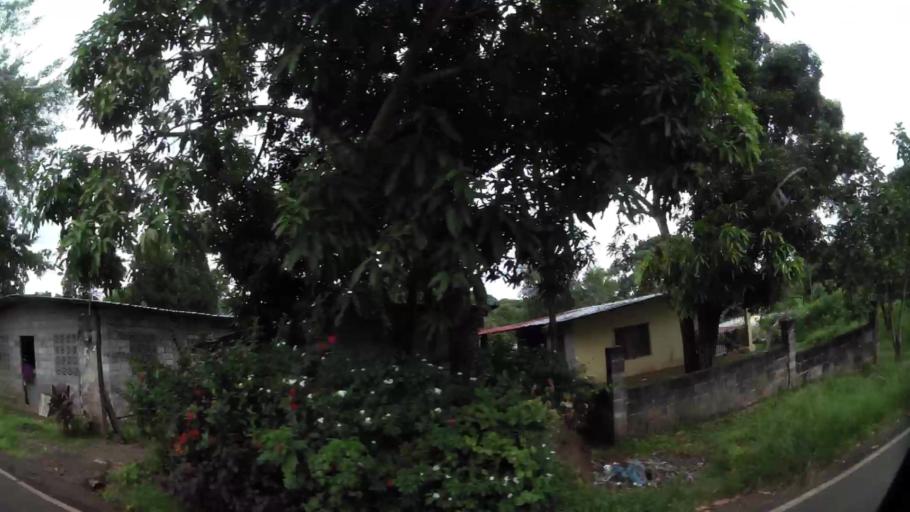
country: PA
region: Panama
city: Tocumen
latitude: 9.1153
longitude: -79.3746
